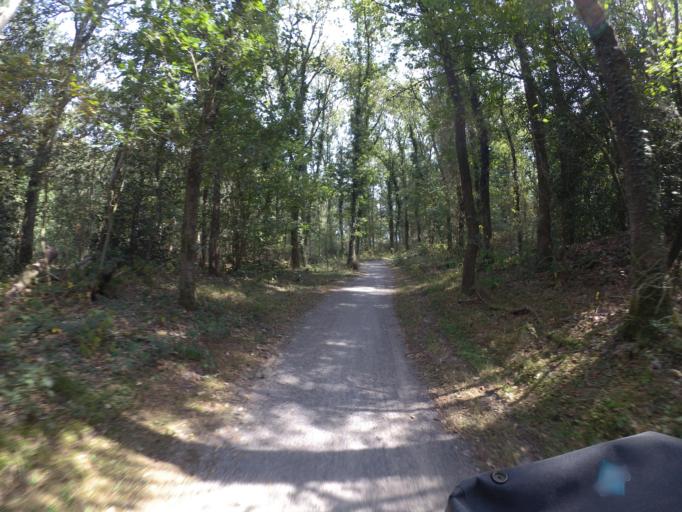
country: NL
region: Drenthe
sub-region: Gemeente Westerveld
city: Havelte
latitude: 52.7994
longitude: 6.2474
